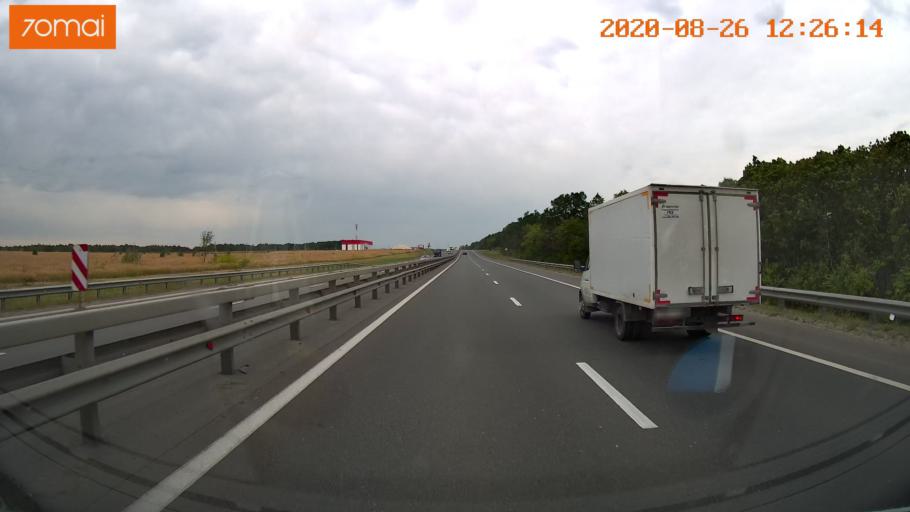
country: RU
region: Rjazan
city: Polyany
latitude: 54.5330
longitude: 39.8638
